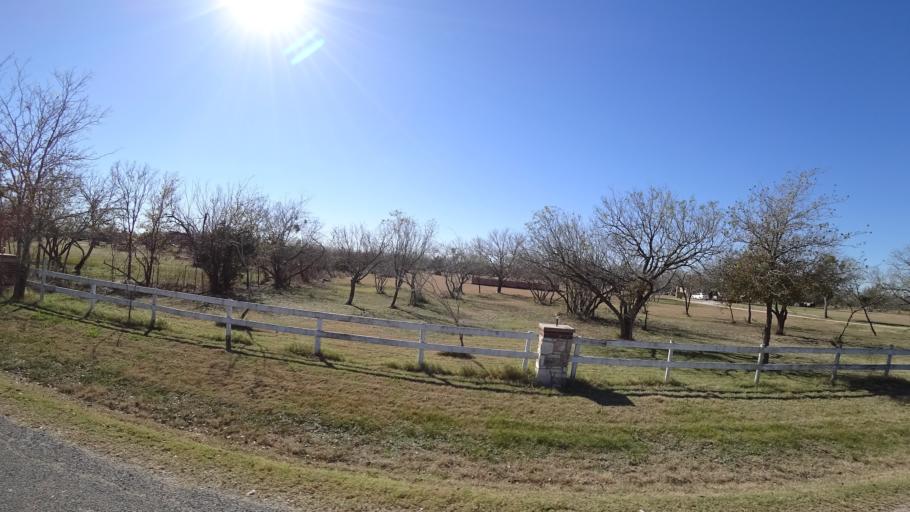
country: US
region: Texas
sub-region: Travis County
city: Garfield
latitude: 30.1257
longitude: -97.6179
